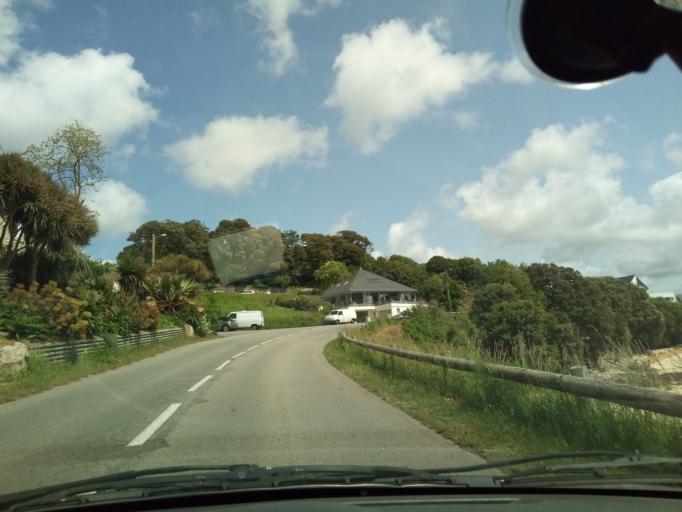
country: FR
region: Brittany
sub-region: Departement du Finistere
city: Audierne
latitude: 48.0170
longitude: -4.5383
